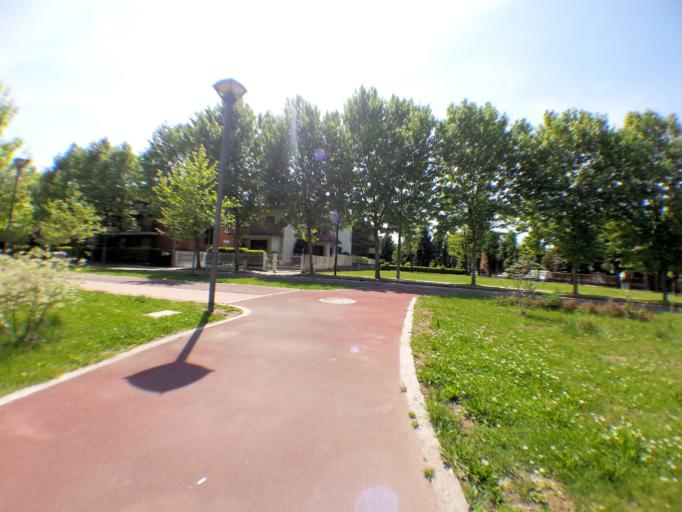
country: IT
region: Lombardy
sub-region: Citta metropolitana di Milano
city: Cusano Milanino
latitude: 45.5514
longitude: 9.1948
